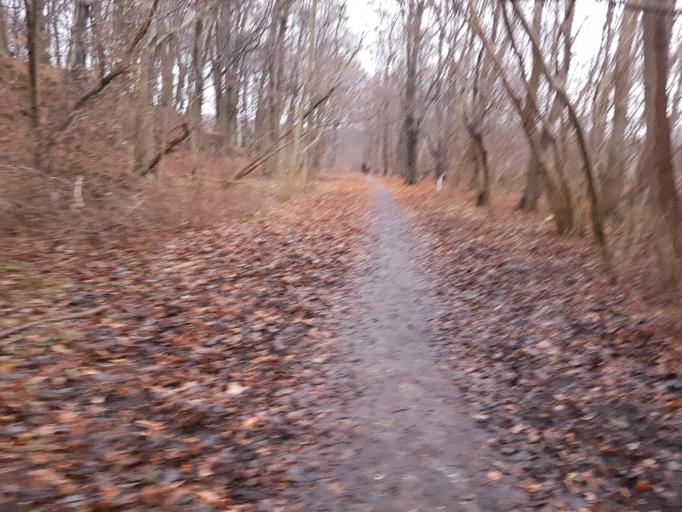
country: DE
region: Mecklenburg-Vorpommern
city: Ostseebad Binz
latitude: 54.3920
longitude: 13.5960
